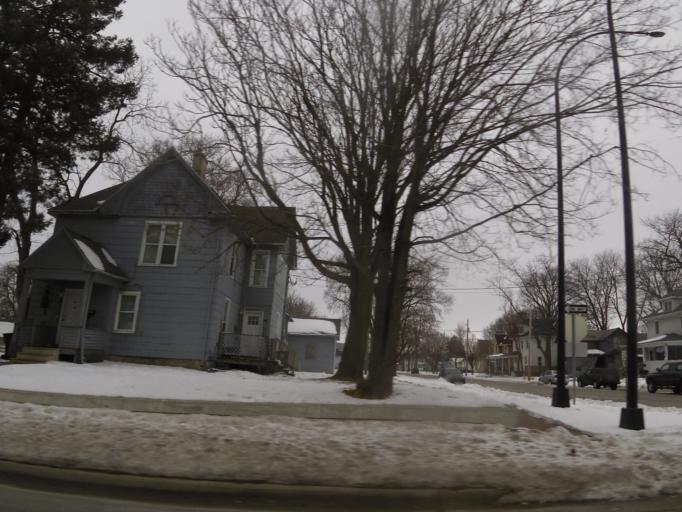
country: US
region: Iowa
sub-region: Black Hawk County
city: Waterloo
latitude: 42.5025
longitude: -92.3404
